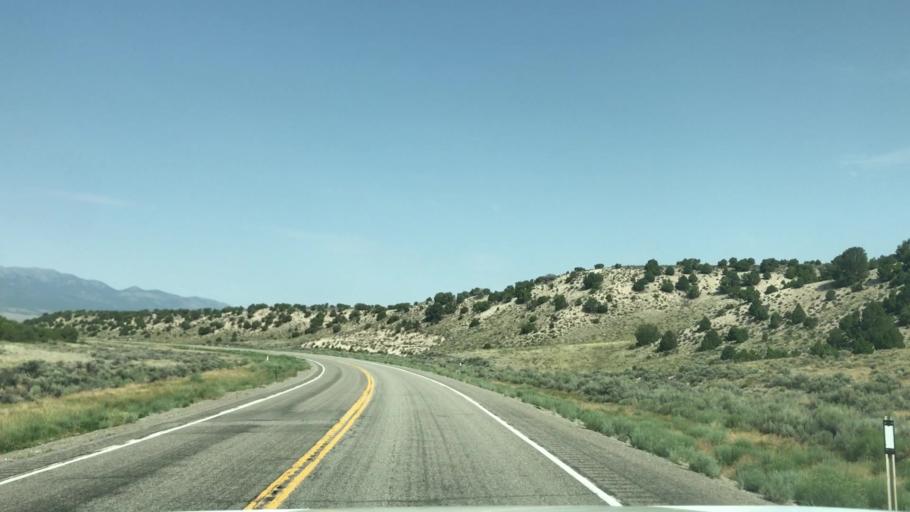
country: US
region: Nevada
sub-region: White Pine County
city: Ely
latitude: 39.0298
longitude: -114.6935
